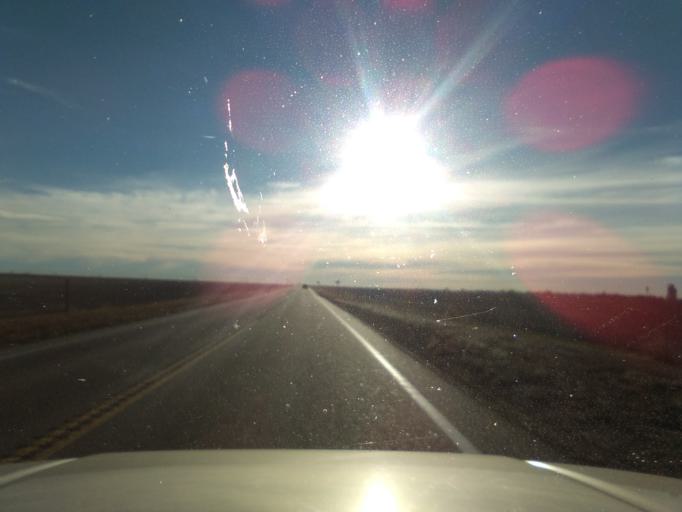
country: US
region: Kansas
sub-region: Sheridan County
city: Hoxie
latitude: 39.4750
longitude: -100.7252
